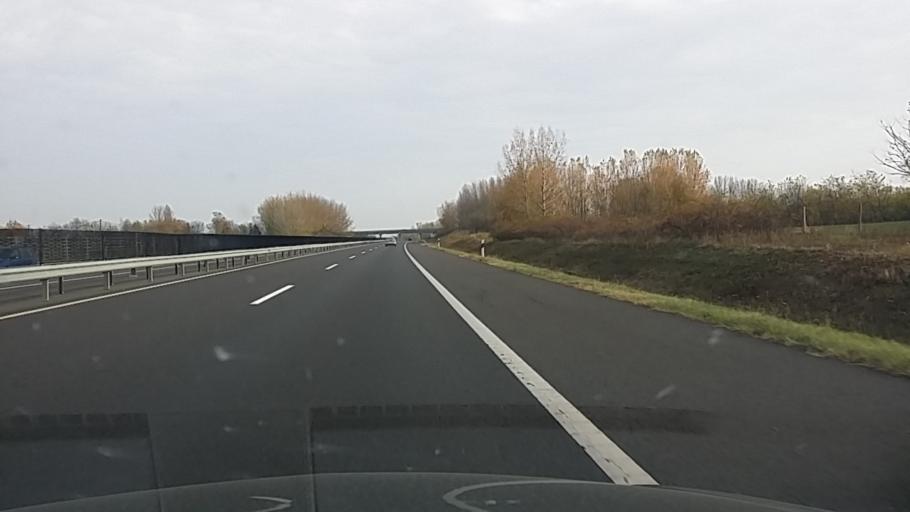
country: HU
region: Szabolcs-Szatmar-Bereg
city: Kalmanhaza
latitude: 47.9011
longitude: 21.5944
